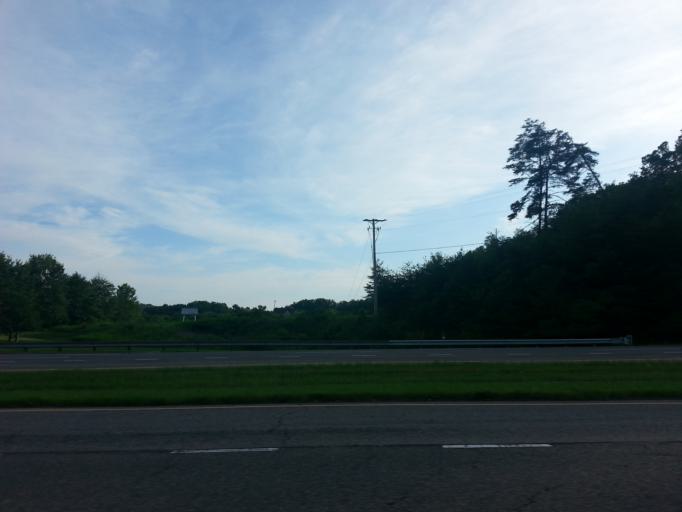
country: US
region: Tennessee
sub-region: Knox County
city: Farragut
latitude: 35.9385
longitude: -84.1490
